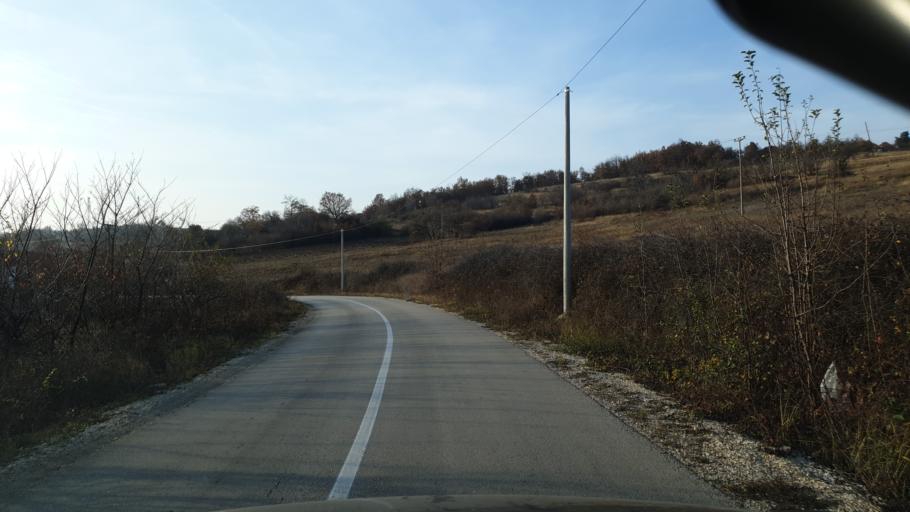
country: RS
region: Central Serbia
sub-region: Borski Okrug
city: Bor
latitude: 44.0490
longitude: 22.0911
